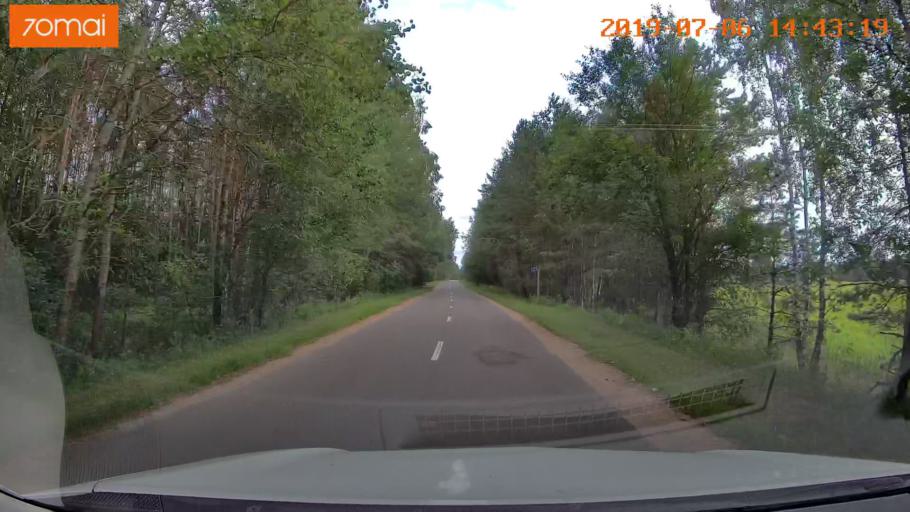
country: BY
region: Minsk
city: Ivyanyets
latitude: 53.9505
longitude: 26.6935
